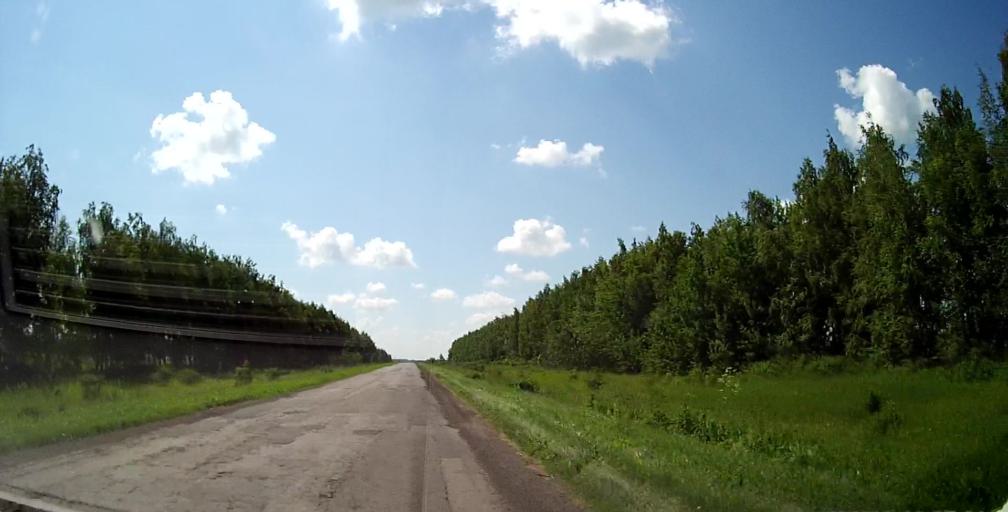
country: RU
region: Lipetsk
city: Chaplygin
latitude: 53.3637
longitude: 39.9188
